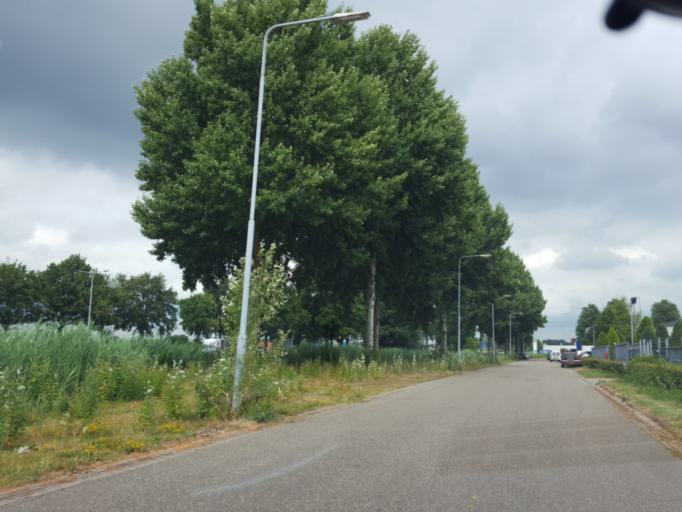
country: NL
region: Limburg
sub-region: Gemeente Weert
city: Weert
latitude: 51.2718
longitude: 5.7247
